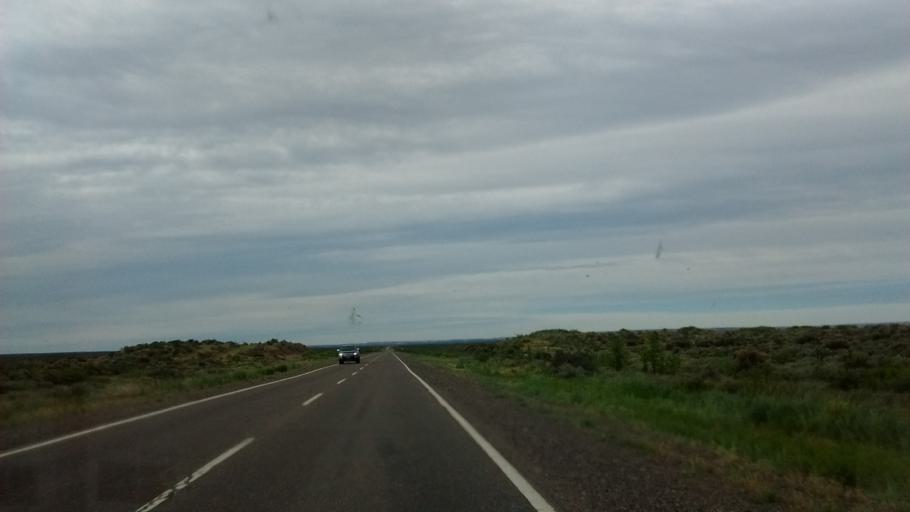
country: AR
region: Rio Negro
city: Catriel
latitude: -38.0386
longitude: -67.9177
